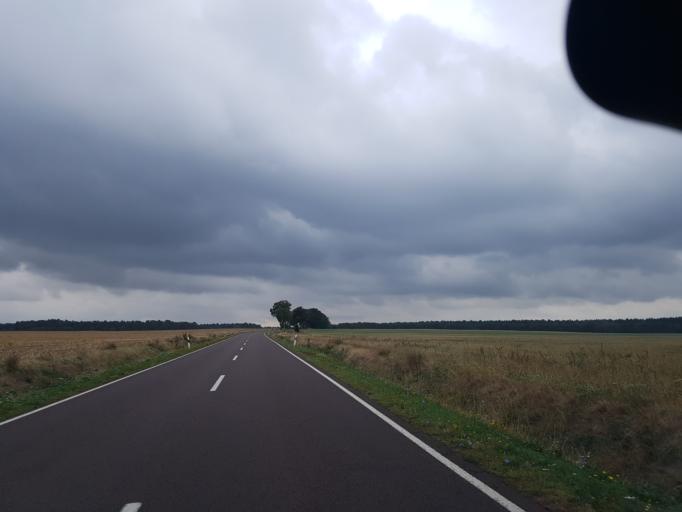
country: DE
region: Saxony-Anhalt
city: Loburg
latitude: 52.1548
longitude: 12.1039
